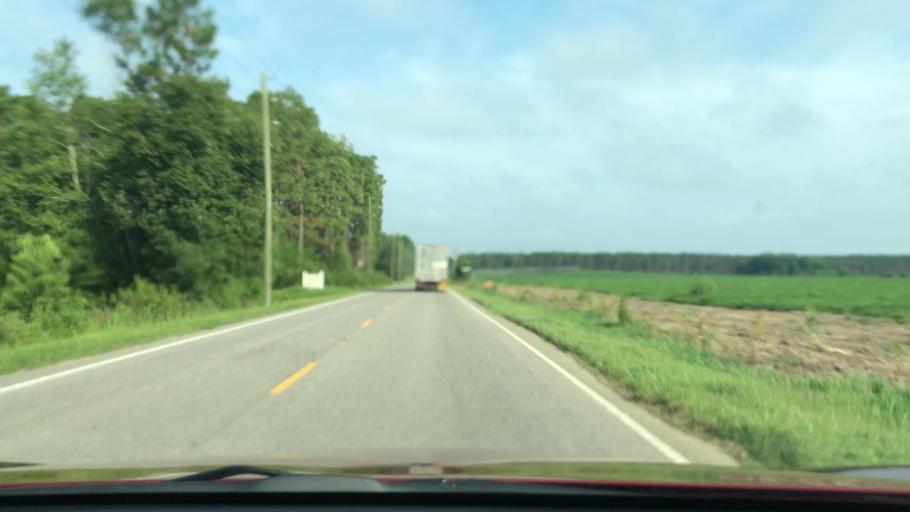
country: US
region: South Carolina
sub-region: Barnwell County
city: Blackville
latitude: 33.6104
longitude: -81.2756
